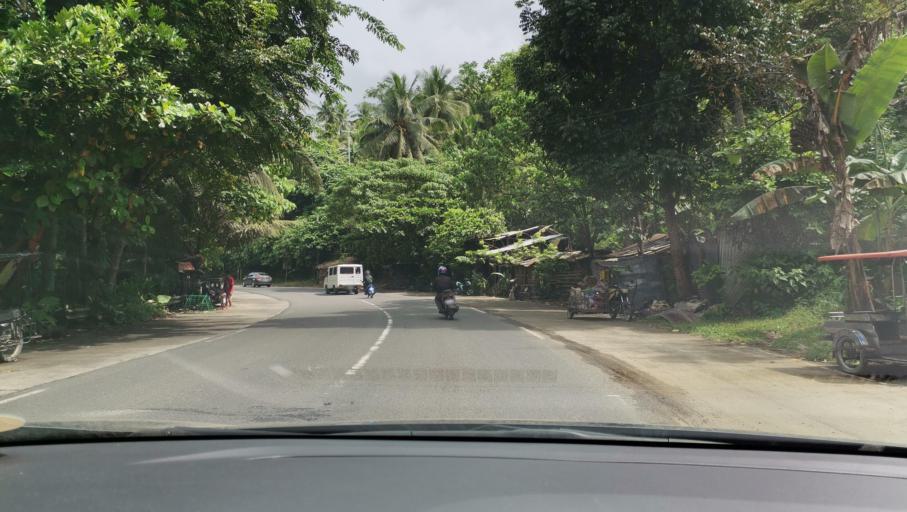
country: PH
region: Calabarzon
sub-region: Province of Quezon
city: Rizal
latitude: 13.9468
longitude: 122.2889
